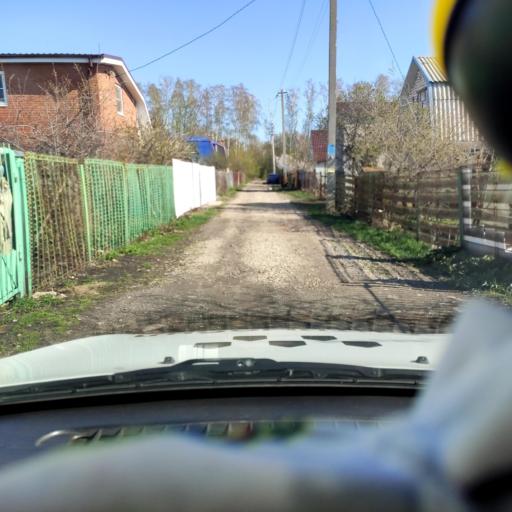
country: RU
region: Samara
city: Tol'yatti
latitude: 53.5992
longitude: 49.2944
